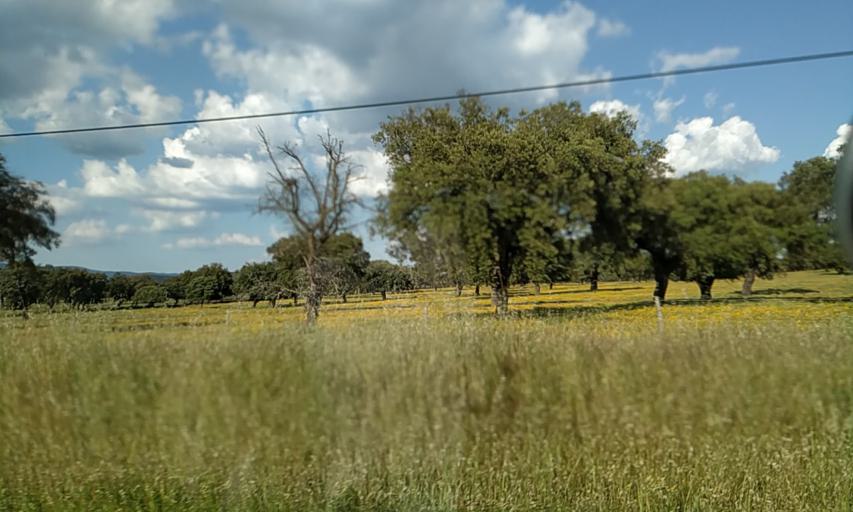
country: PT
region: Portalegre
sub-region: Portalegre
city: Urra
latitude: 39.1806
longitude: -7.4548
